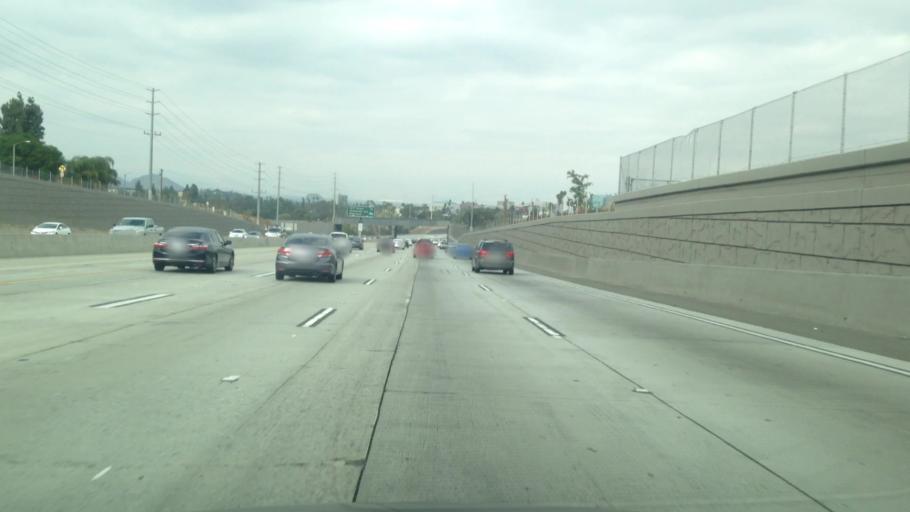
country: US
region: California
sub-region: Riverside County
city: Riverside
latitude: 33.9615
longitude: -117.3775
